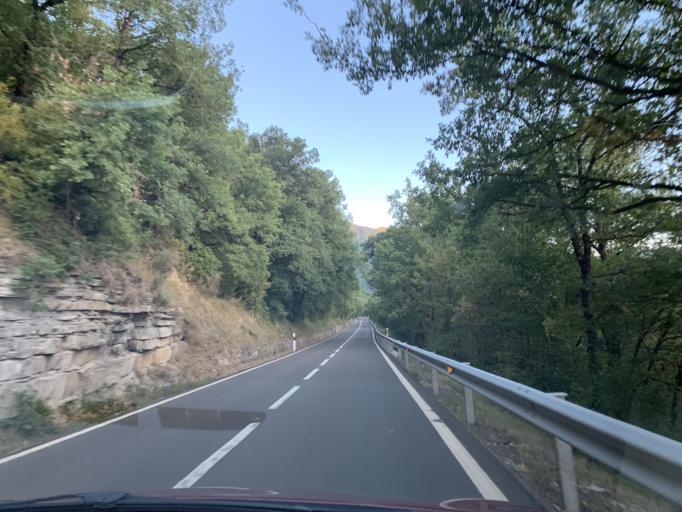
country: ES
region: Aragon
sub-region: Provincia de Huesca
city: Broto
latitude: 42.5896
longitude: -0.1180
